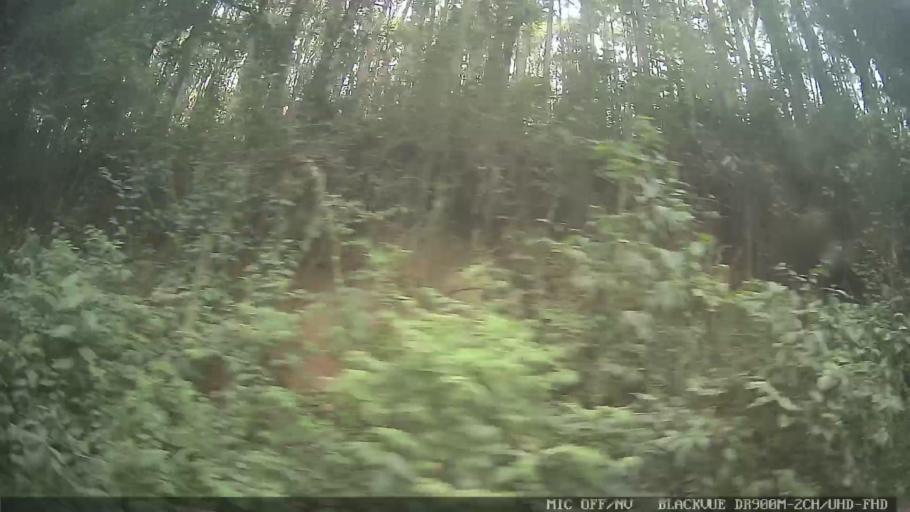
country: BR
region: Sao Paulo
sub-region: Atibaia
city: Atibaia
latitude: -23.1637
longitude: -46.5159
